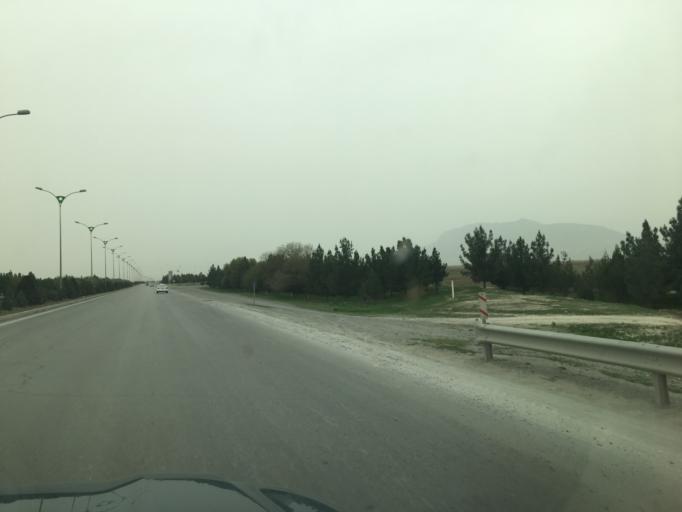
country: TM
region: Ahal
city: Abadan
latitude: 38.1468
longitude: 57.9885
